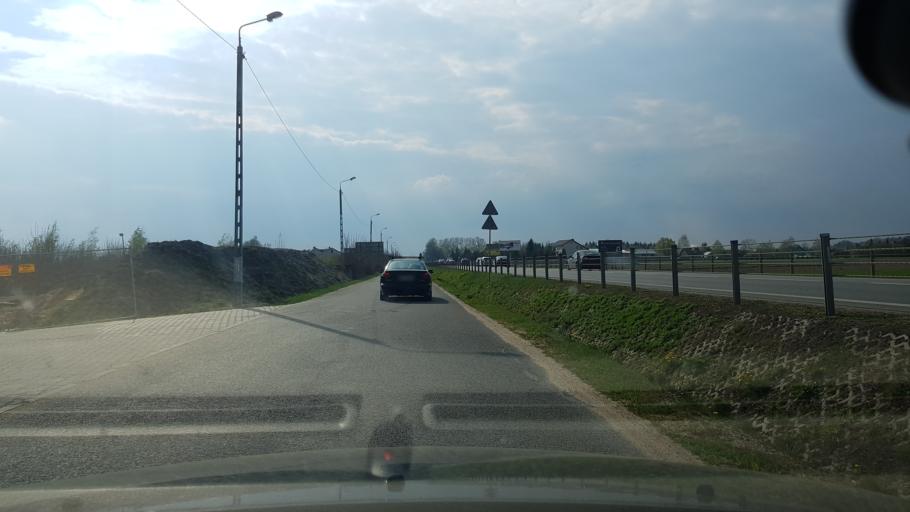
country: PL
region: Masovian Voivodeship
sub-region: Powiat minski
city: Debe Wielkie
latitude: 52.1999
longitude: 21.4692
